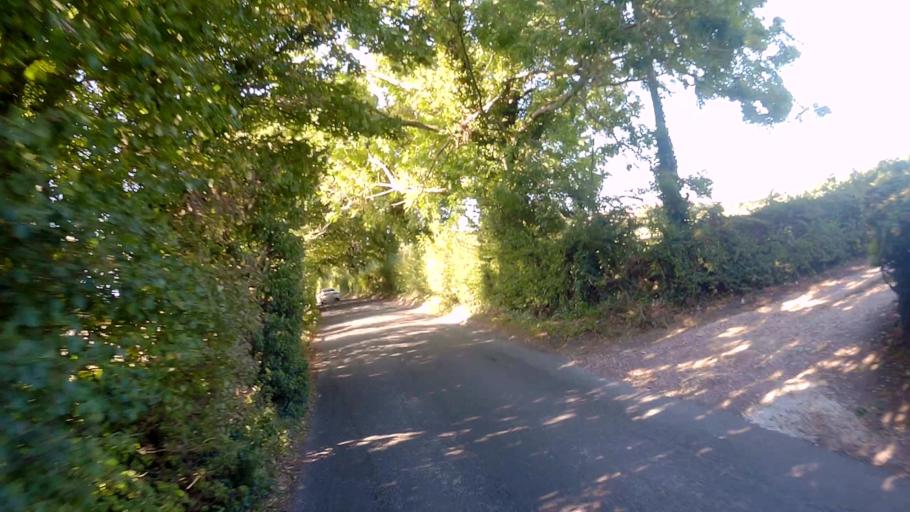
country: GB
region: England
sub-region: Hampshire
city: Long Sutton
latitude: 51.1865
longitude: -0.9012
